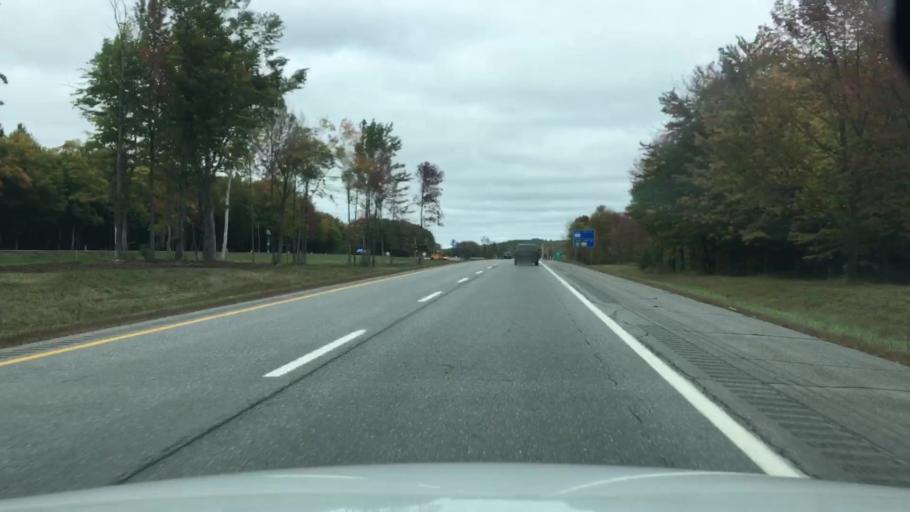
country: US
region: Maine
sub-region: Somerset County
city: Fairfield
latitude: 44.5867
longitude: -69.6216
